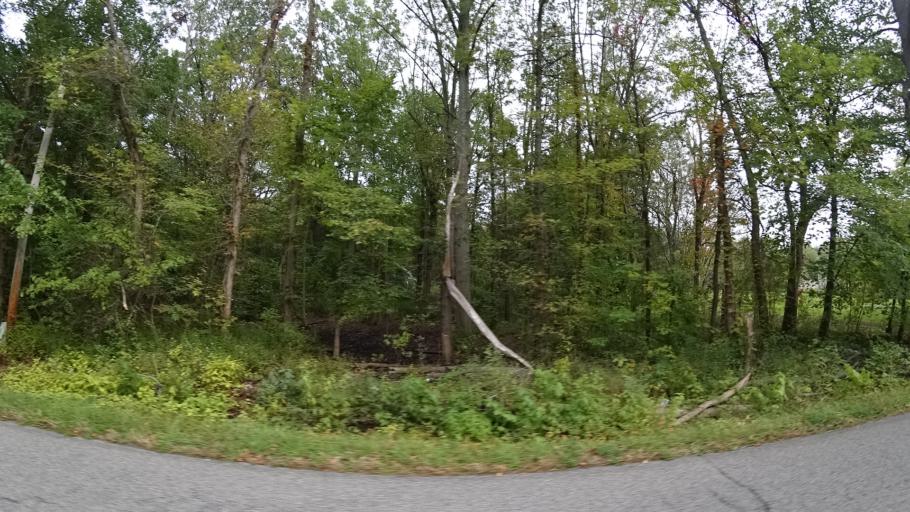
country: US
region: Indiana
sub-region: LaPorte County
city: Long Beach
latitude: 41.7297
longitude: -86.8162
